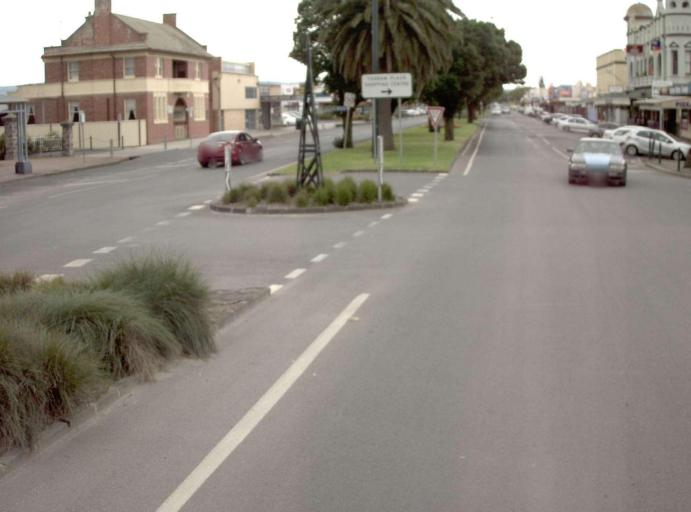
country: AU
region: Victoria
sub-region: Latrobe
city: Traralgon
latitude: -38.5653
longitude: 146.6756
